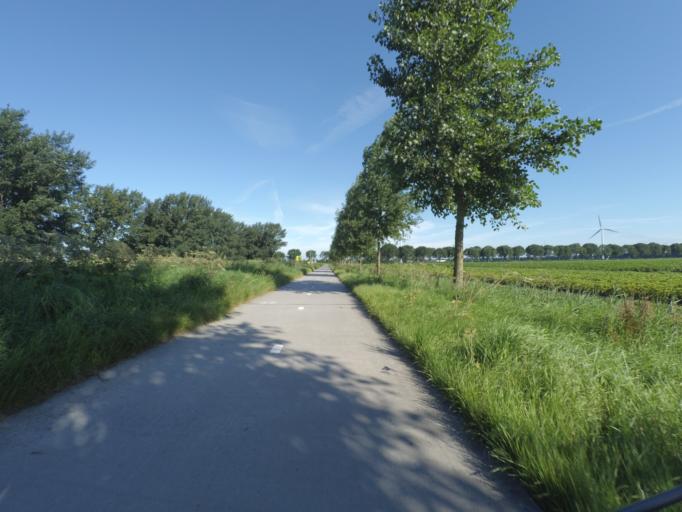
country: NL
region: Flevoland
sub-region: Gemeente Zeewolde
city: Zeewolde
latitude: 52.3610
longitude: 5.4834
